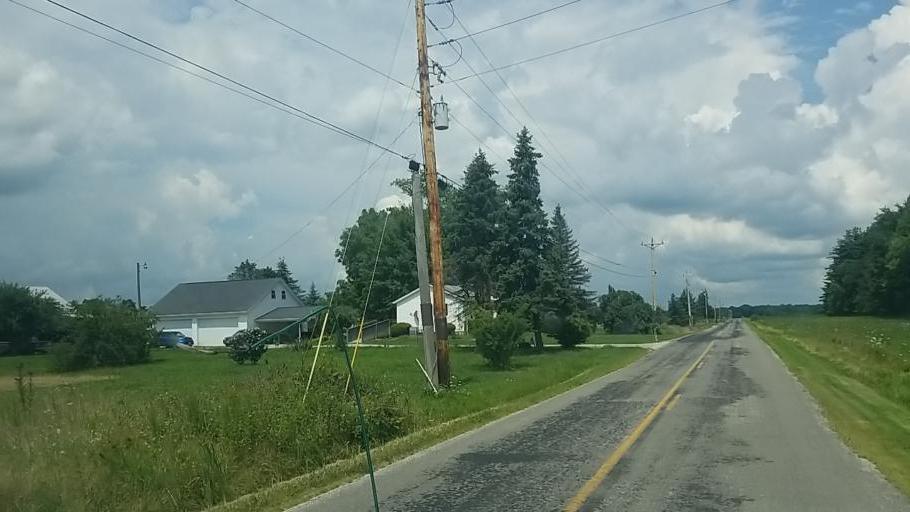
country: US
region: Ohio
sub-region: Medina County
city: Lodi
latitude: 41.1256
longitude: -82.0745
